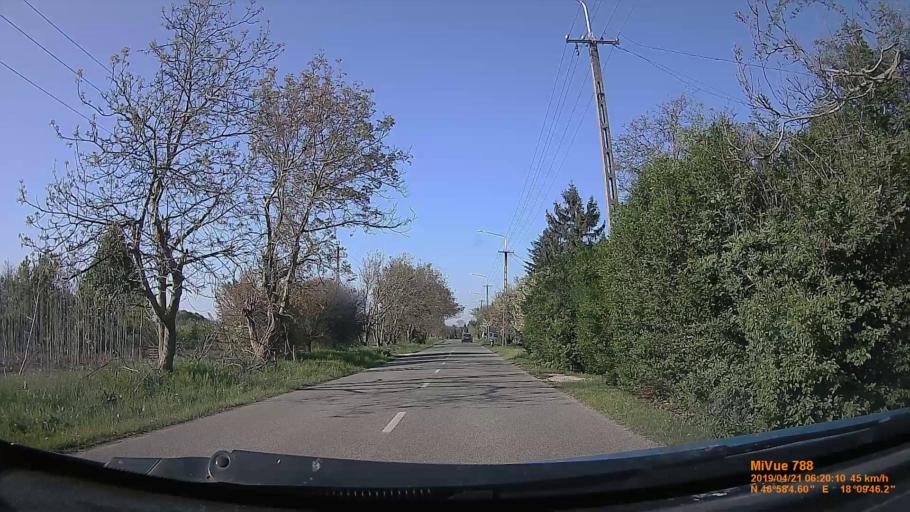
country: HU
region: Somogy
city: Balatonszabadi
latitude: 46.9680
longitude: 18.1629
